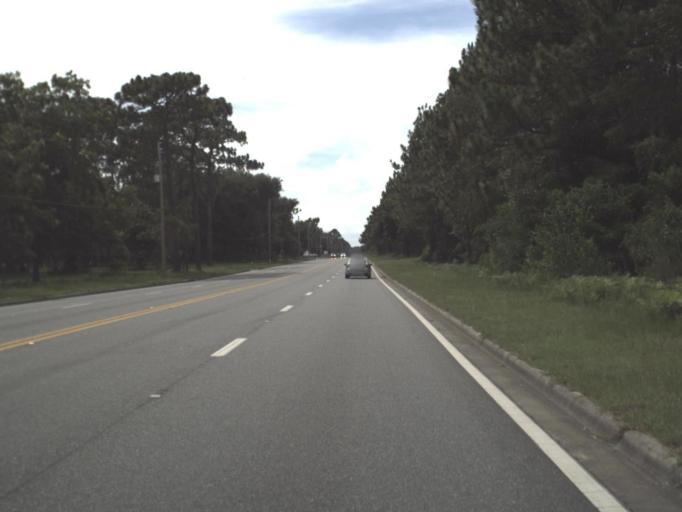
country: US
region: Florida
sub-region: Taylor County
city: Perry
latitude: 30.0988
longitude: -83.5514
